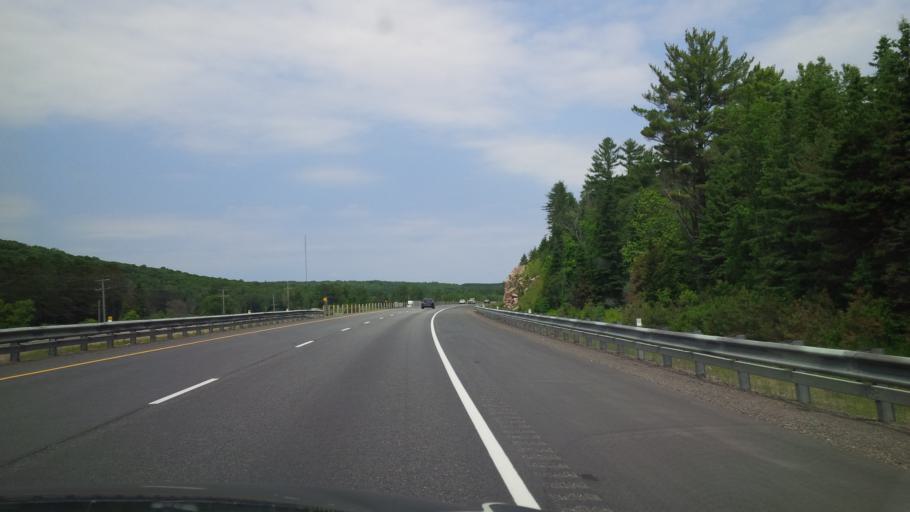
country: CA
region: Ontario
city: Huntsville
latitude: 45.3916
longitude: -79.2347
